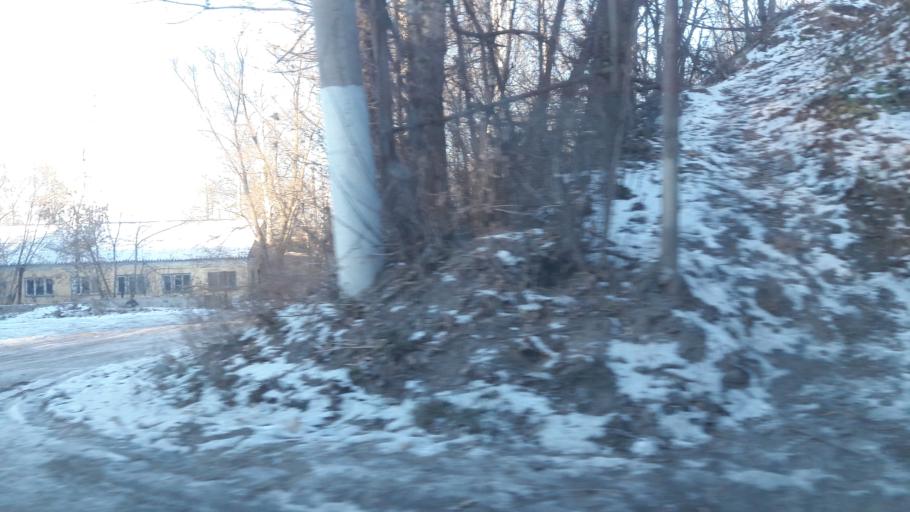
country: RU
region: Tula
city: Tula
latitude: 54.2177
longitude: 37.6474
